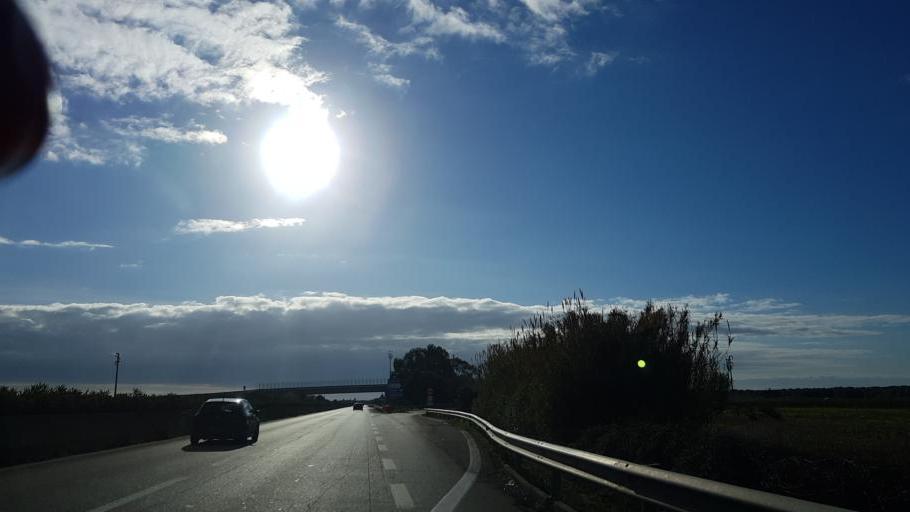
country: IT
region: Apulia
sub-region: Provincia di Brindisi
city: Tuturano
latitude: 40.5563
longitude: 17.9925
